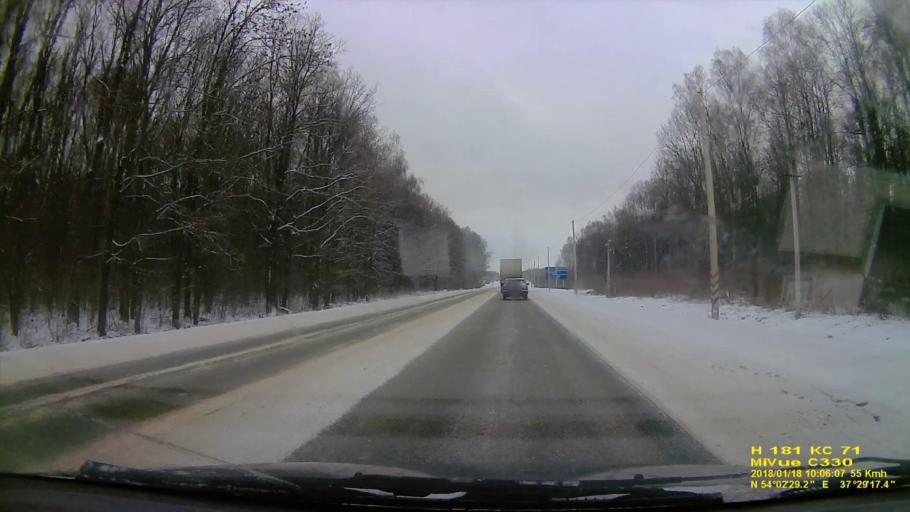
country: RU
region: Tula
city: Pervomayskiy
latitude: 54.0412
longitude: 37.4881
